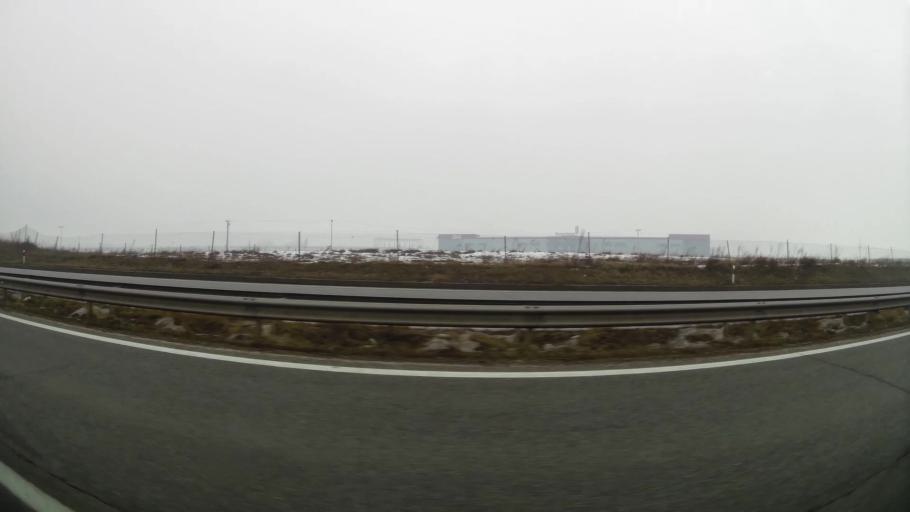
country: MK
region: Petrovec
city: Petrovec
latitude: 41.9477
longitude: 21.6307
